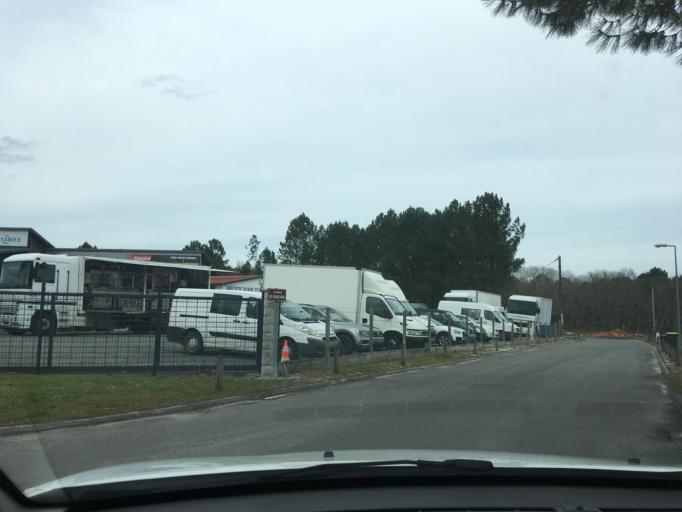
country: FR
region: Aquitaine
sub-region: Departement de la Gironde
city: Saint-Sauveur
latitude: 45.2210
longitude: -0.8725
